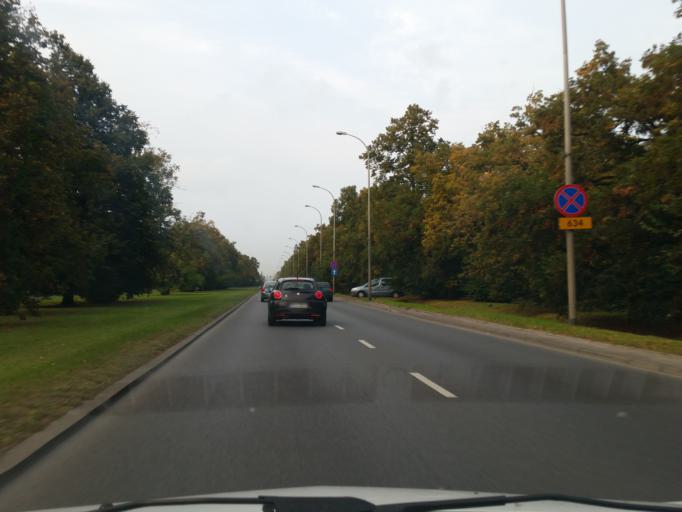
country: PL
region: Masovian Voivodeship
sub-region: Warszawa
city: Wlochy
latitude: 52.1845
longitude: 20.9793
